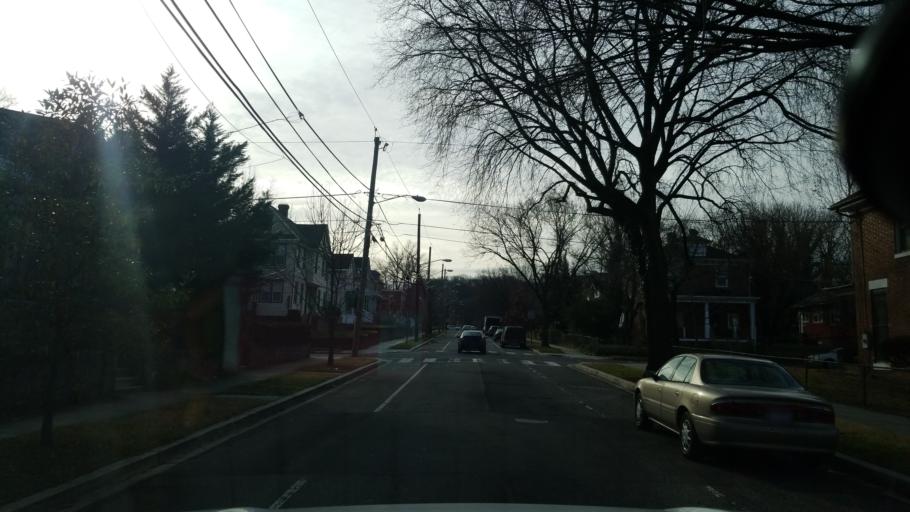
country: US
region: Maryland
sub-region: Prince George's County
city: Silver Hill
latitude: 38.8711
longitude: -76.9709
